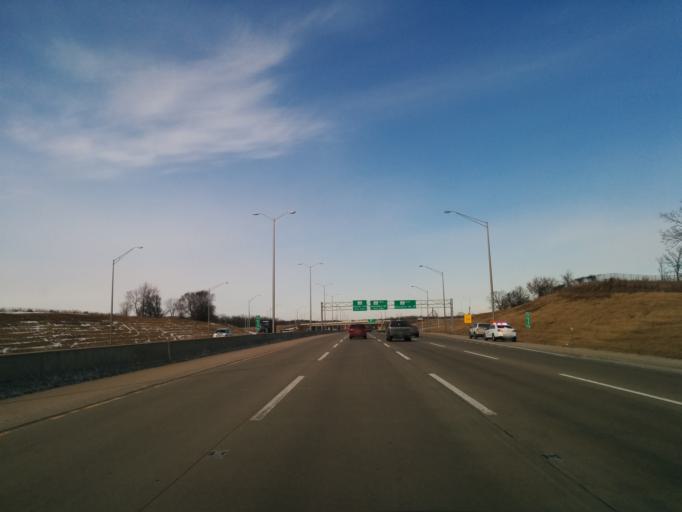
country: US
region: Illinois
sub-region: Lake County
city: Gurnee
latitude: 42.3416
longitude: -87.9196
